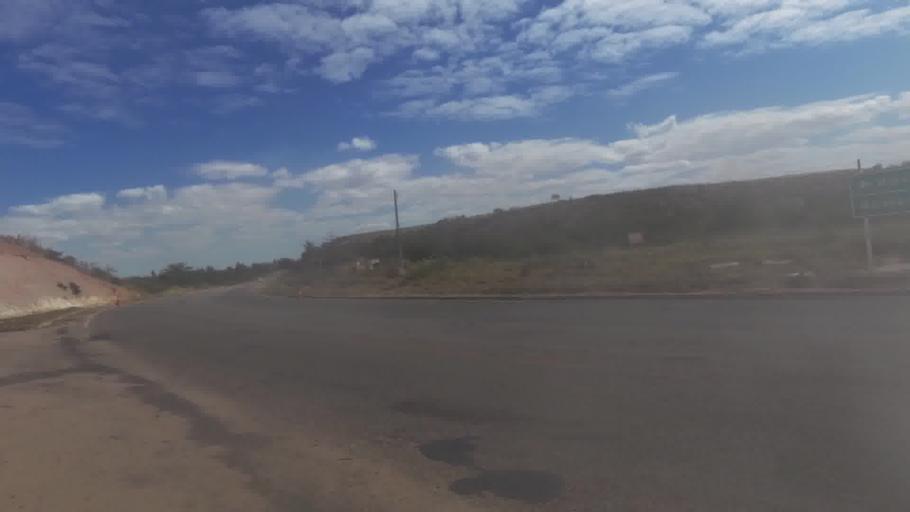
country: BR
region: Espirito Santo
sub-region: Marataizes
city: Marataizes
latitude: -21.1850
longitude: -40.9259
